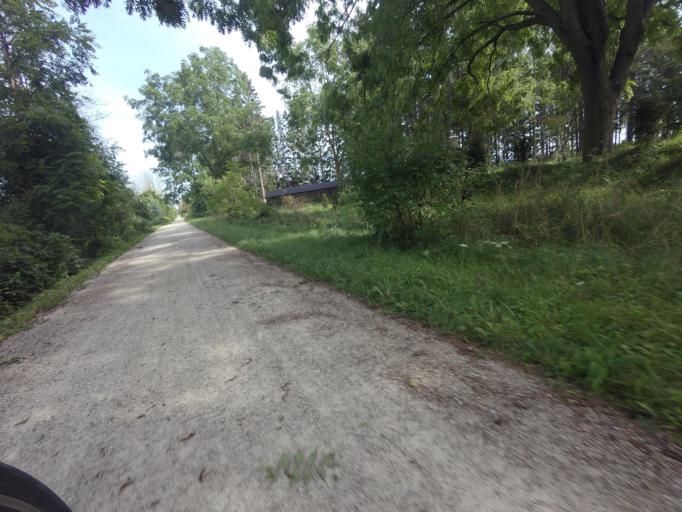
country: CA
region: Ontario
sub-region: Wellington County
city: Guelph
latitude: 43.5766
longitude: -80.3734
